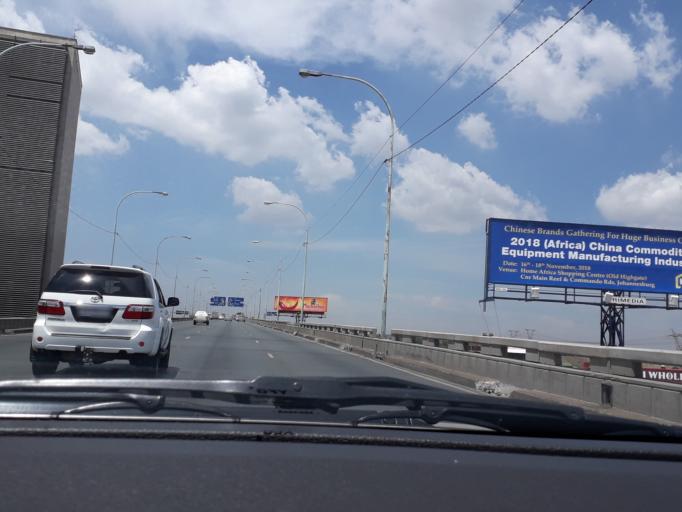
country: ZA
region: Gauteng
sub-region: City of Johannesburg Metropolitan Municipality
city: Johannesburg
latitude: -26.2062
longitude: 28.0306
